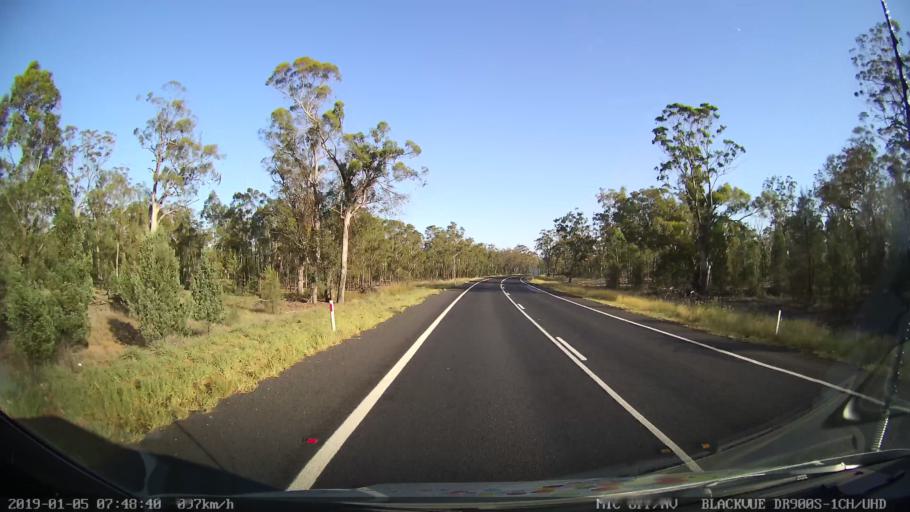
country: AU
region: New South Wales
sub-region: Gilgandra
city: Gilgandra
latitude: -31.8131
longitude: 148.6370
